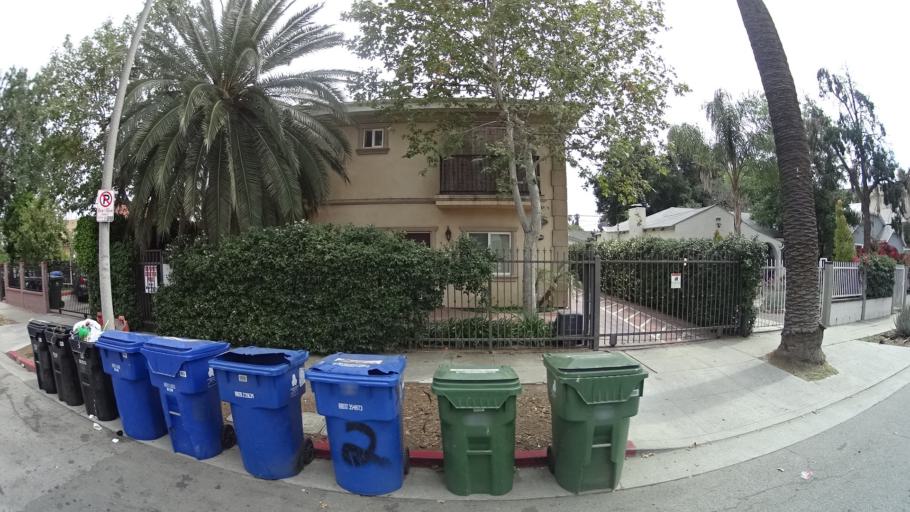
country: US
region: California
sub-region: Los Angeles County
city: Van Nuys
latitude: 34.1857
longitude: -118.4554
